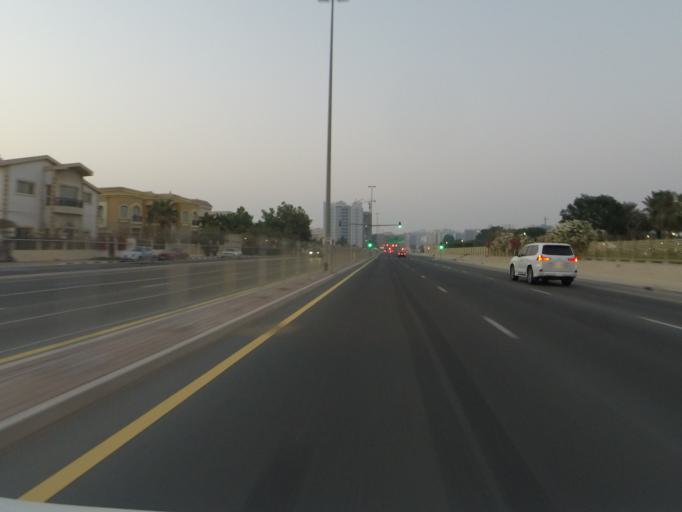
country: AE
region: Dubai
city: Dubai
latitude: 25.1012
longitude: 55.1996
